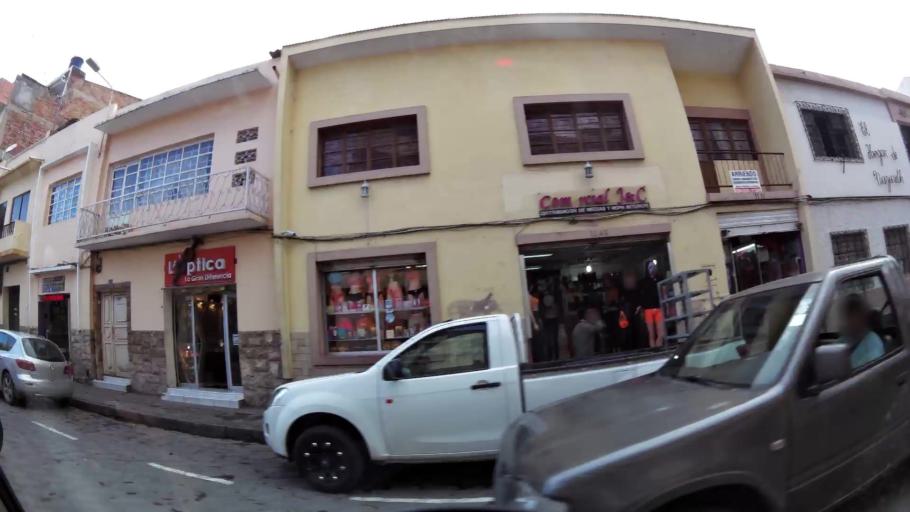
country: EC
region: Azuay
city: Cuenca
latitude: -2.8957
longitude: -78.9986
